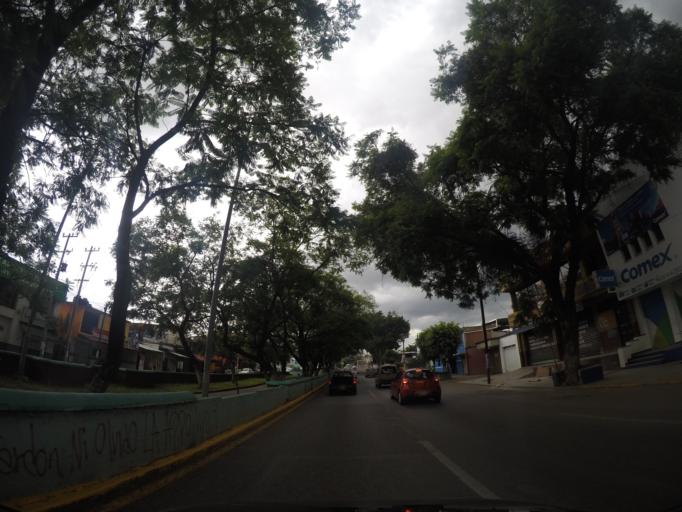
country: MX
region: Oaxaca
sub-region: Santa Cruz Amilpas
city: Santa Cruz Amilpas
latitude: 17.0694
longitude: -96.7006
